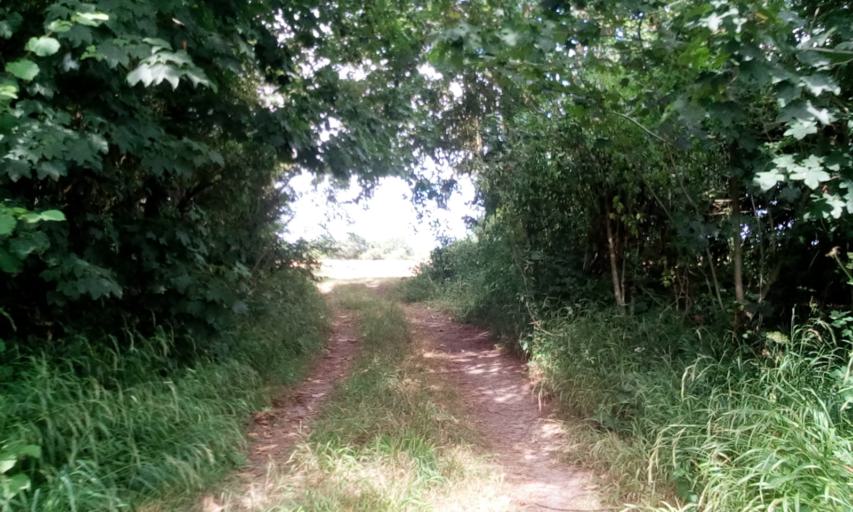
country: FR
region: Lower Normandy
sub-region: Departement du Calvados
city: Sannerville
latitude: 49.1567
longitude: -0.2068
